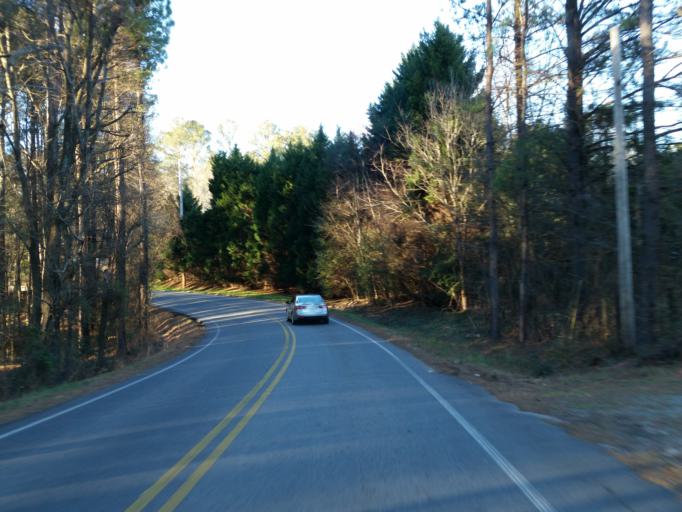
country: US
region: Georgia
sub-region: Cherokee County
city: Holly Springs
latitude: 34.1256
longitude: -84.4446
